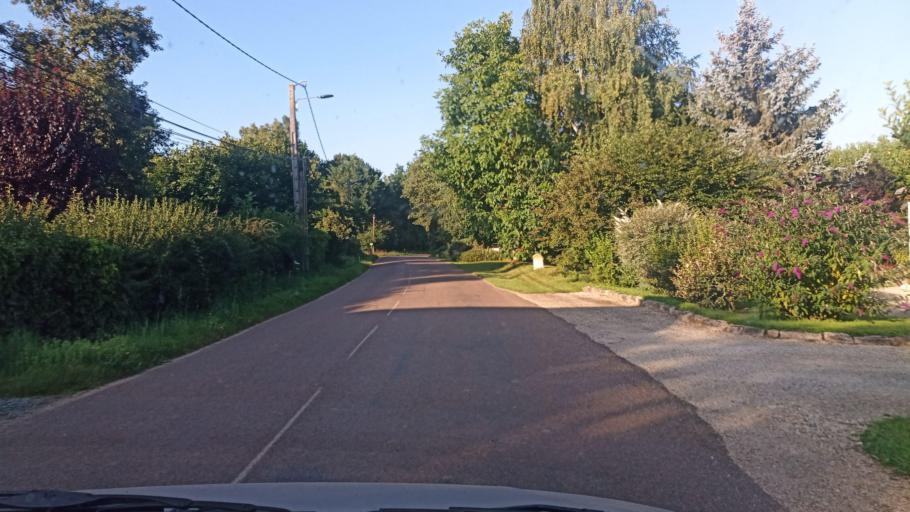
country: FR
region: Bourgogne
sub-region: Departement de l'Yonne
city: Saint-Valerien
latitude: 48.1902
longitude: 3.1159
